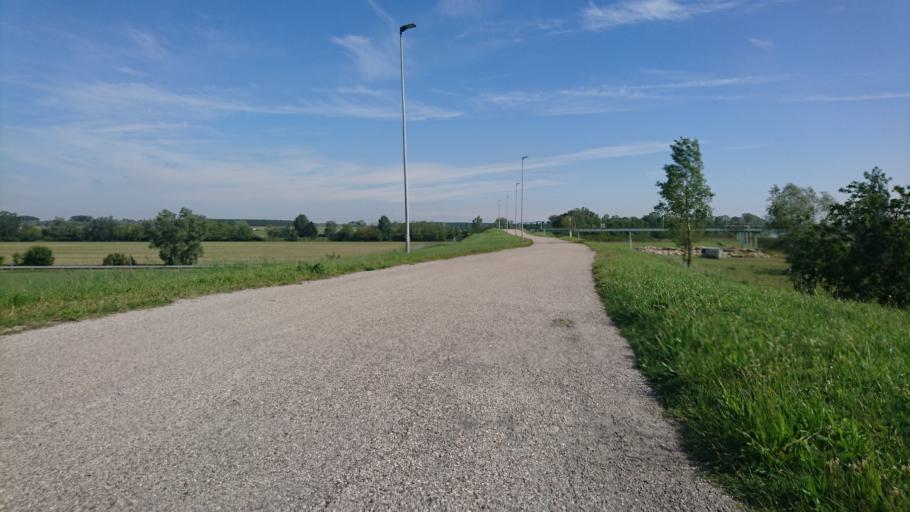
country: IT
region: Veneto
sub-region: Provincia di Rovigo
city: Castelnovo Bariano
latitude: 45.0283
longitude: 11.2582
